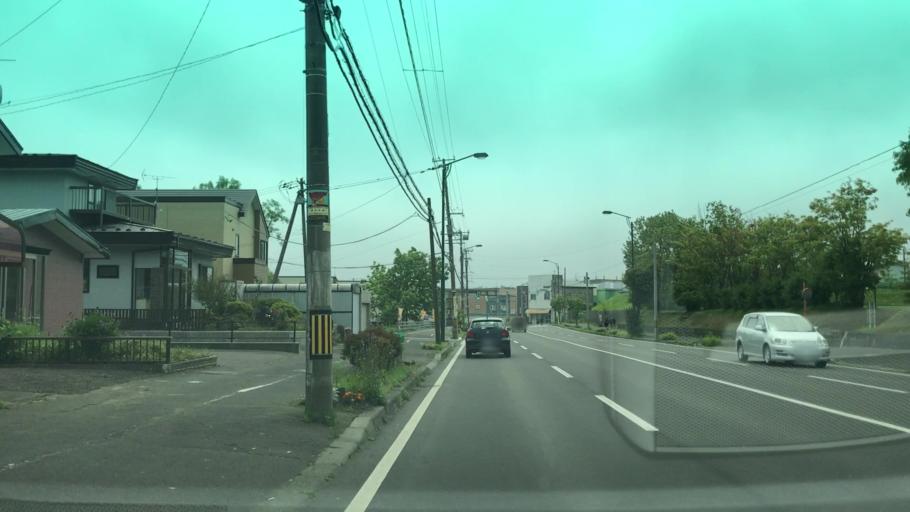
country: JP
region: Hokkaido
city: Muroran
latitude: 42.3668
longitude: 141.0364
